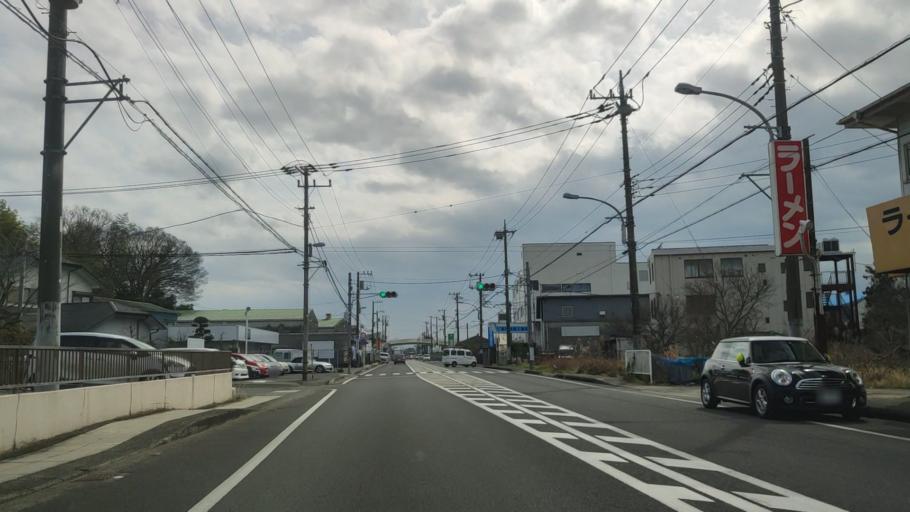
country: JP
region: Kanagawa
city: Odawara
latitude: 35.3117
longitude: 139.1628
